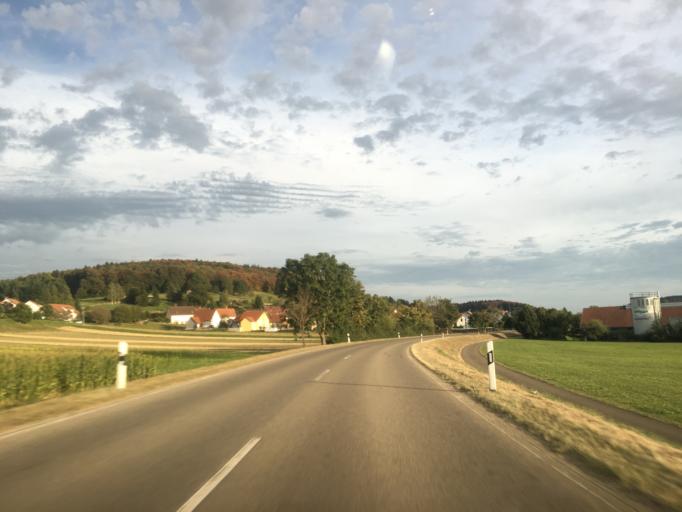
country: DE
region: Baden-Wuerttemberg
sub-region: Tuebingen Region
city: Sankt Johann
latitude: 48.4625
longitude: 9.3396
